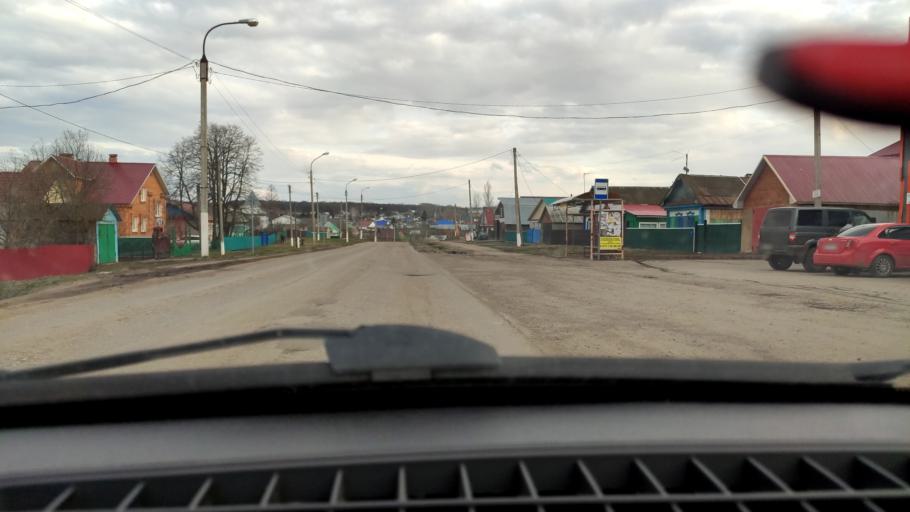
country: RU
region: Bashkortostan
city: Tolbazy
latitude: 54.0253
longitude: 55.8855
